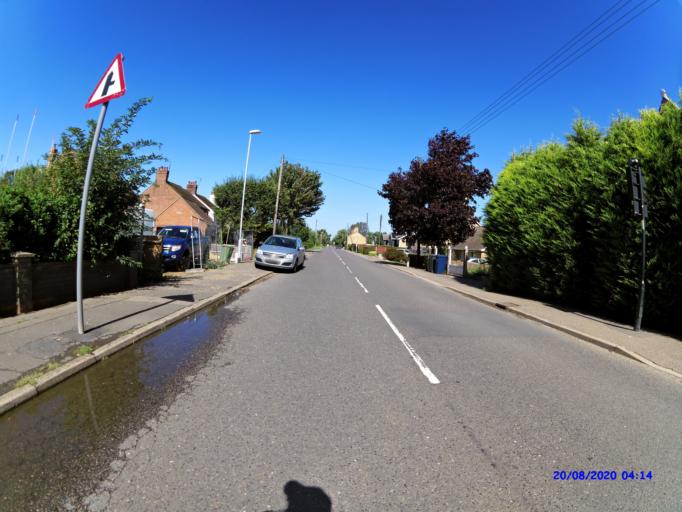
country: GB
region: England
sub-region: Cambridgeshire
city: Ramsey
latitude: 52.4850
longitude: -0.1087
